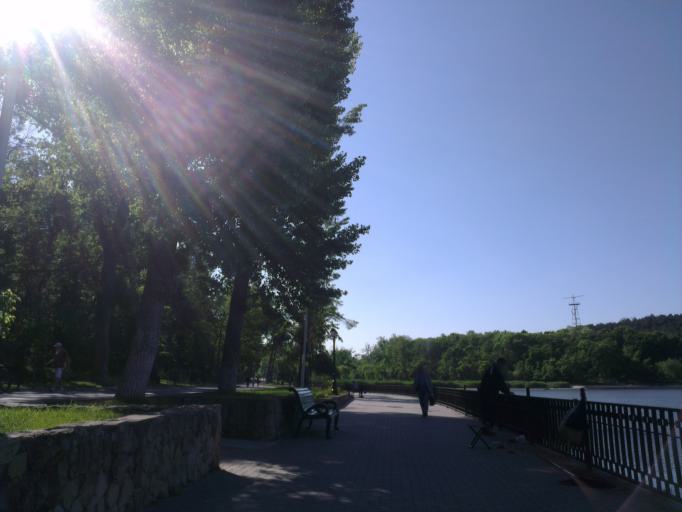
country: MD
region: Chisinau
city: Chisinau
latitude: 47.0204
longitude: 28.8160
